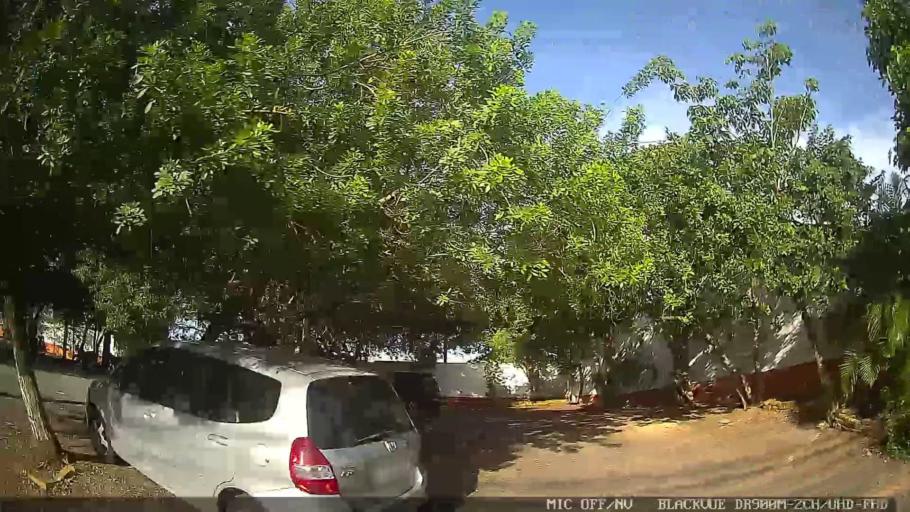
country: BR
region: Sao Paulo
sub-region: Tiete
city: Tiete
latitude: -23.0748
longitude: -47.7266
